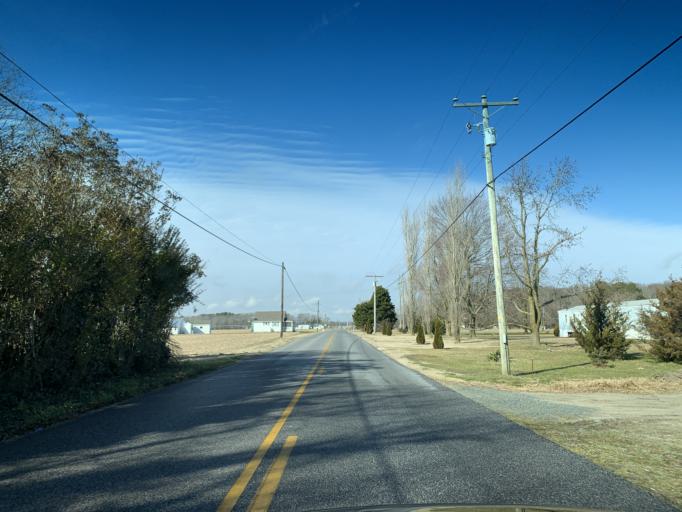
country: US
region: Maryland
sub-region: Worcester County
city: Ocean Pines
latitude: 38.4268
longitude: -75.1729
